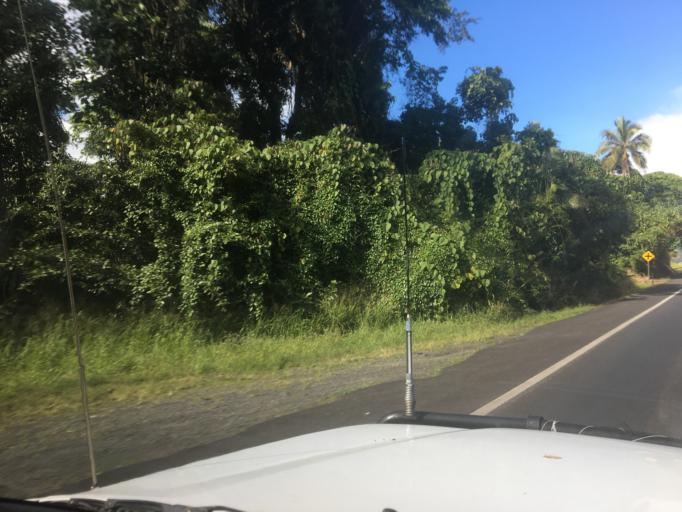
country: AU
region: Queensland
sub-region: Cassowary Coast
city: Innisfail
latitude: -17.2604
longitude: 145.9214
